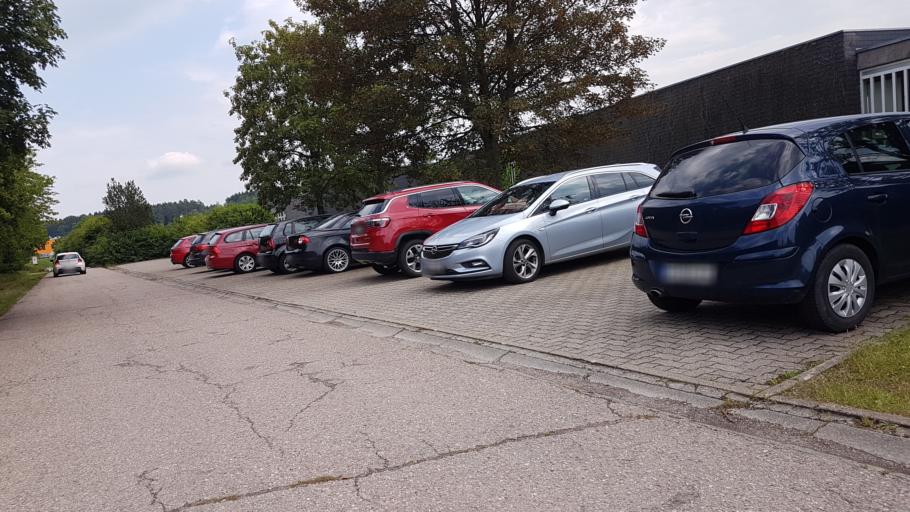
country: DE
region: Baden-Wuerttemberg
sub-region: Freiburg Region
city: Hufingen
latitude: 47.9212
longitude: 8.4981
